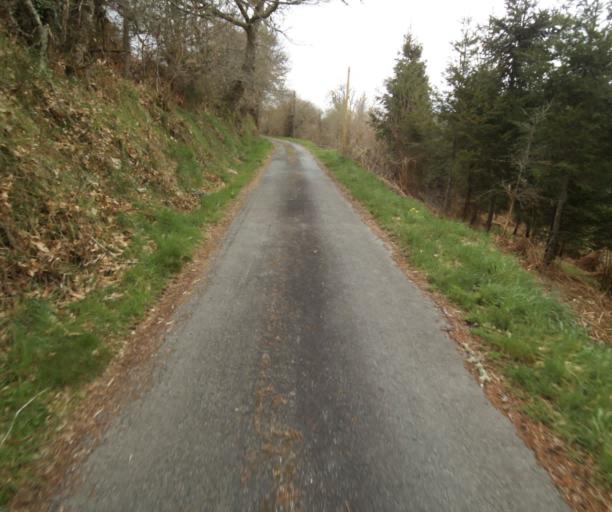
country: FR
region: Limousin
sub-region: Departement de la Correze
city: Correze
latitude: 45.3142
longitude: 1.8895
